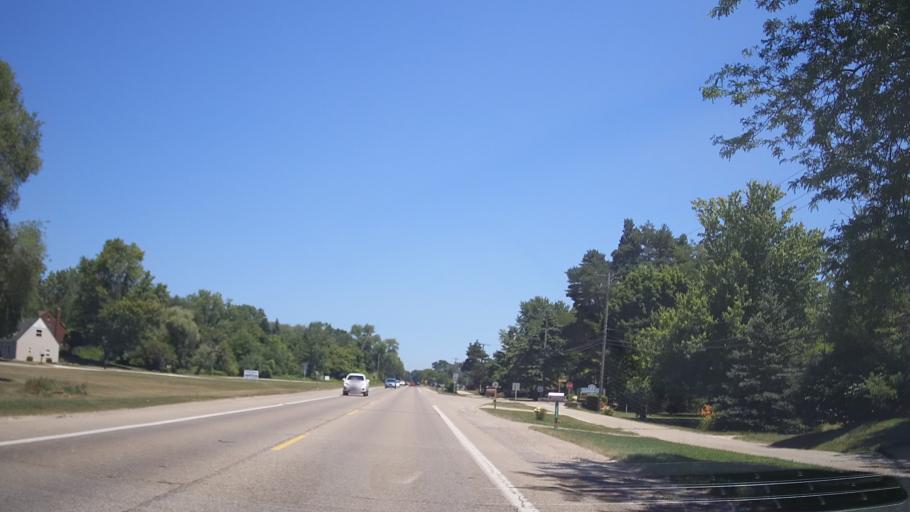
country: US
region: Michigan
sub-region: Macomb County
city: New Baltimore
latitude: 42.6633
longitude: -82.7660
